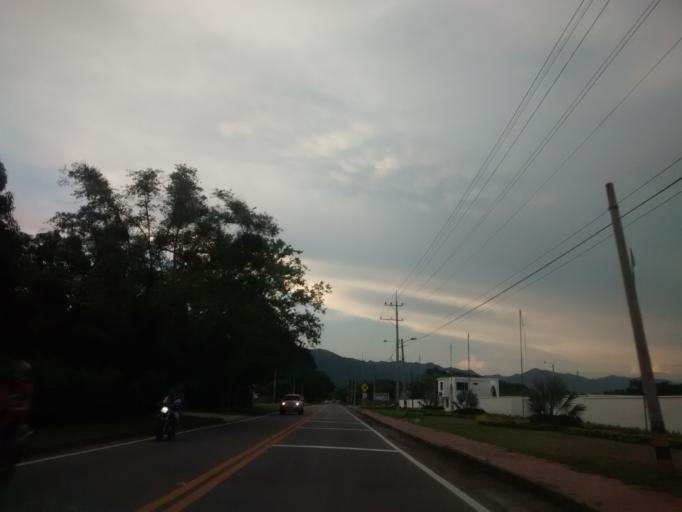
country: CO
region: Cundinamarca
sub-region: Girardot
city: Girardot City
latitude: 4.3412
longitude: -74.8042
